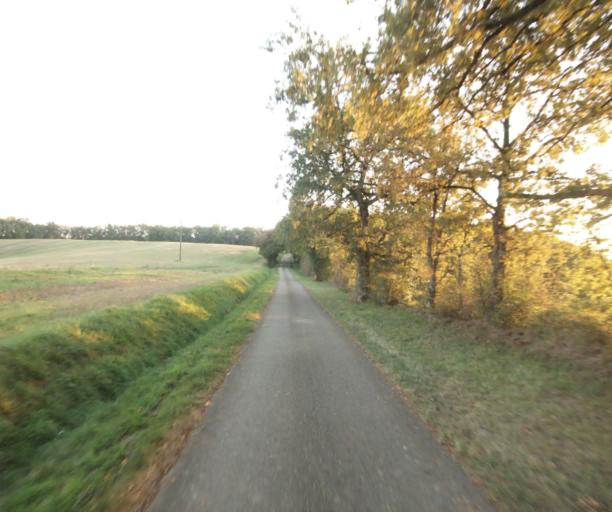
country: FR
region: Midi-Pyrenees
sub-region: Departement du Gers
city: Vic-Fezensac
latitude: 43.7760
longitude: 0.2005
